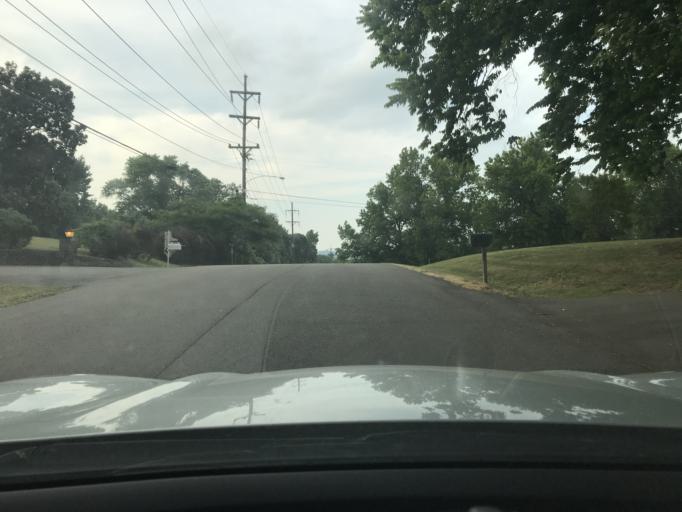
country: US
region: Tennessee
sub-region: Davidson County
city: Goodlettsville
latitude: 36.3087
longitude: -86.7121
